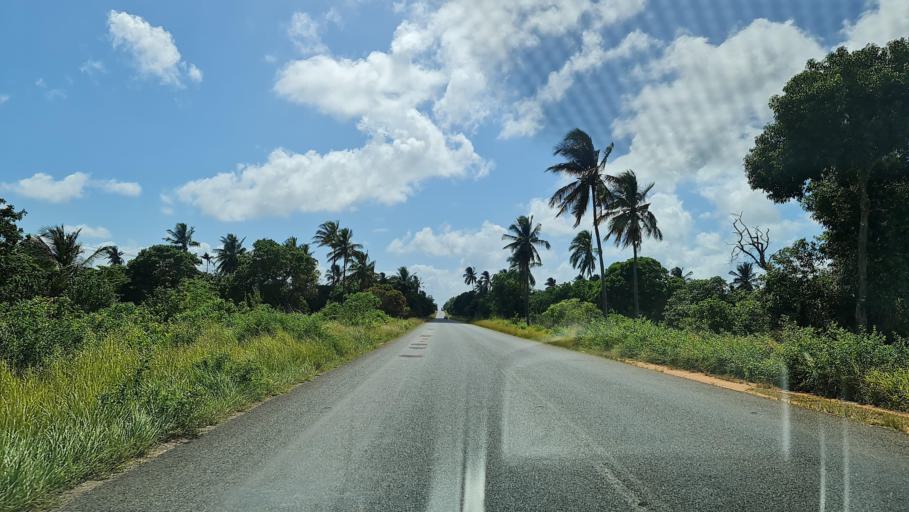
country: MZ
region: Inhambane
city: Maxixe
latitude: -24.5391
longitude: 34.9351
